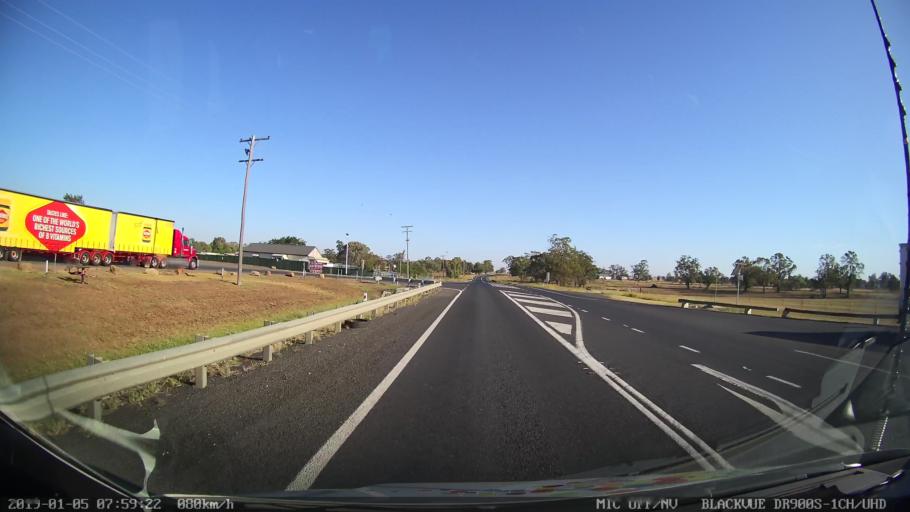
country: AU
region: New South Wales
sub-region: Gilgandra
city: Gilgandra
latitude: -31.7034
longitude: 148.6791
